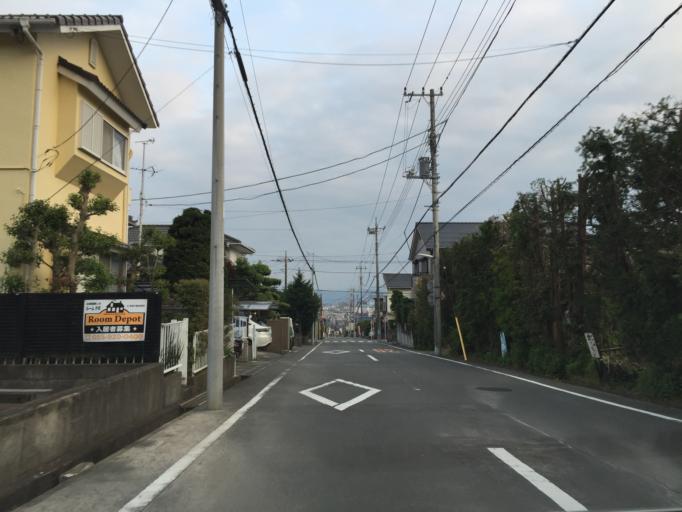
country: JP
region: Shizuoka
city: Numazu
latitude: 35.1303
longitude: 138.8581
